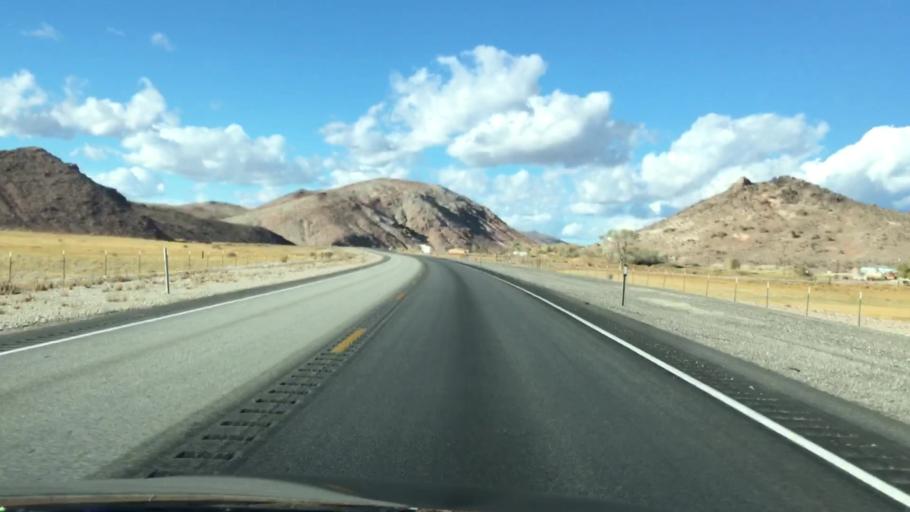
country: US
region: Nevada
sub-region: Nye County
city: Beatty
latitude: 36.9683
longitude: -116.7197
